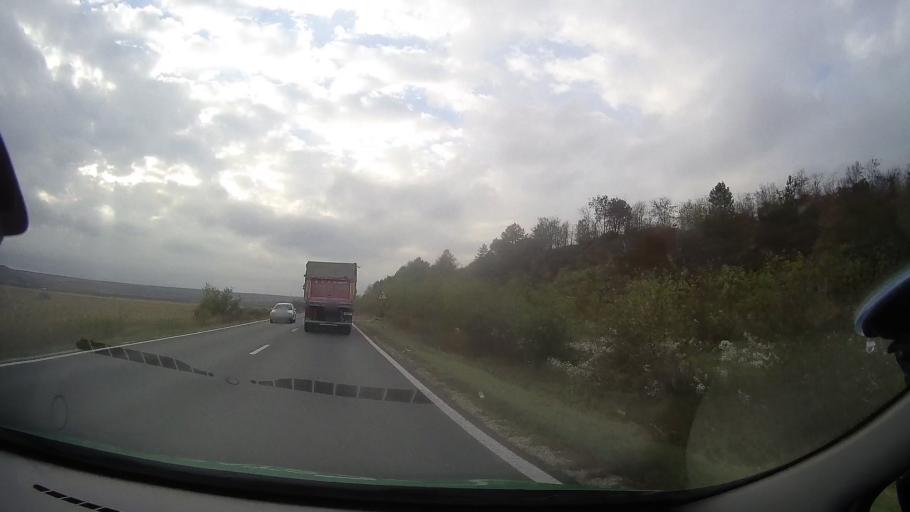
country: RO
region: Constanta
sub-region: Comuna Mircea Voda
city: Mircea Voda
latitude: 44.2685
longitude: 28.1852
